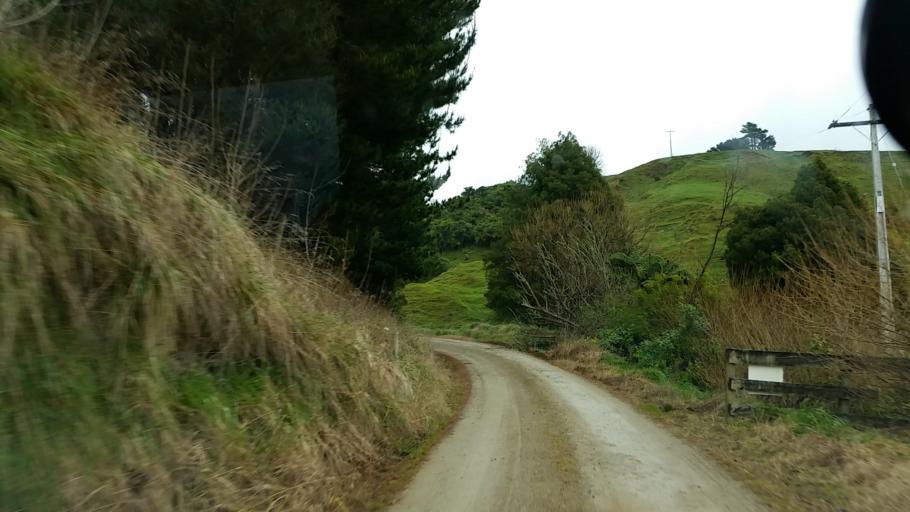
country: NZ
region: Taranaki
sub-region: South Taranaki District
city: Patea
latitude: -39.7577
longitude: 174.7080
